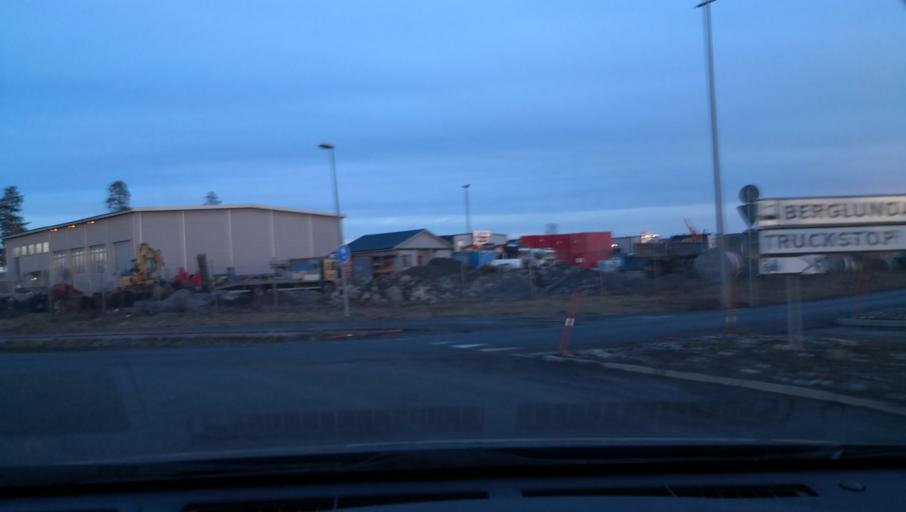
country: SE
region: OErebro
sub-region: Orebro Kommun
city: Orebro
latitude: 59.2378
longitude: 15.1206
